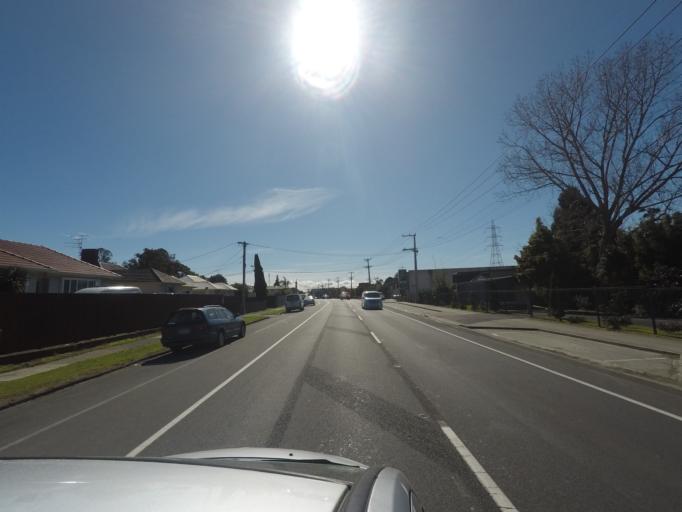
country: NZ
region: Auckland
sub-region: Auckland
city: Waitakere
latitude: -36.9162
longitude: 174.6910
